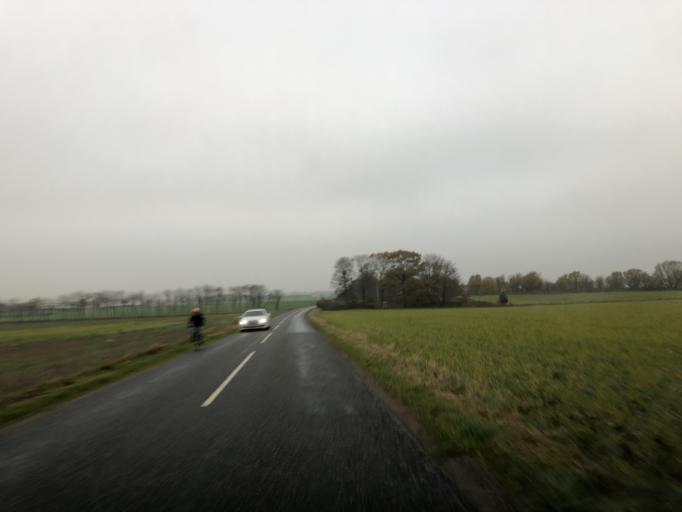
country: DK
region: Central Jutland
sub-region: Herning Kommune
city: Avlum
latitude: 56.2522
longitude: 8.8090
